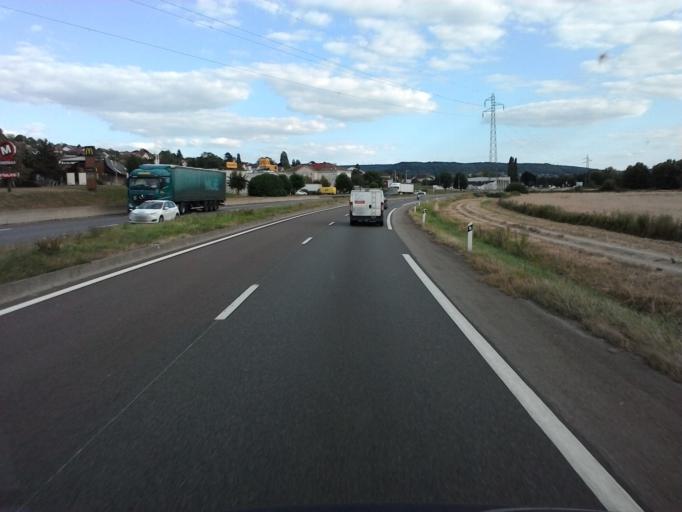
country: FR
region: Franche-Comte
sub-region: Departement de la Haute-Saone
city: Noidans-les-Vesoul
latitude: 47.6323
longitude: 6.1376
